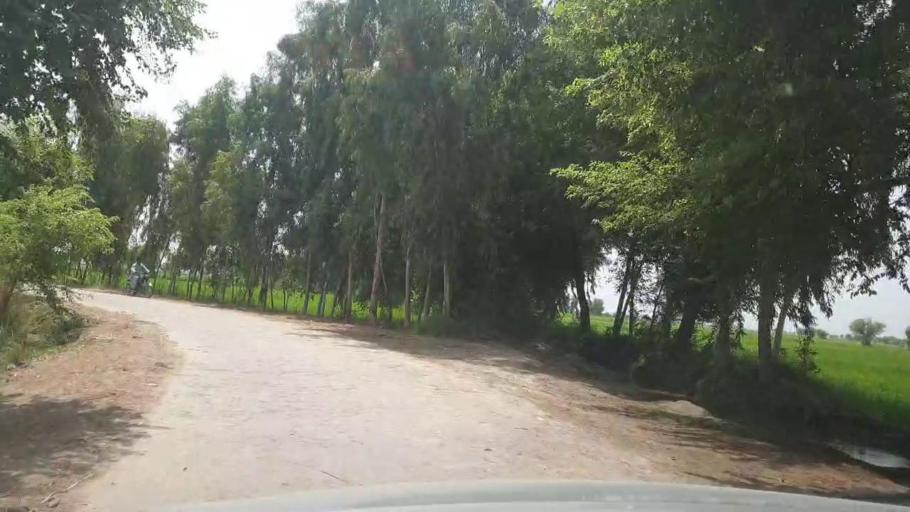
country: PK
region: Sindh
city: Garhi Yasin
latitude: 27.9423
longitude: 68.3764
